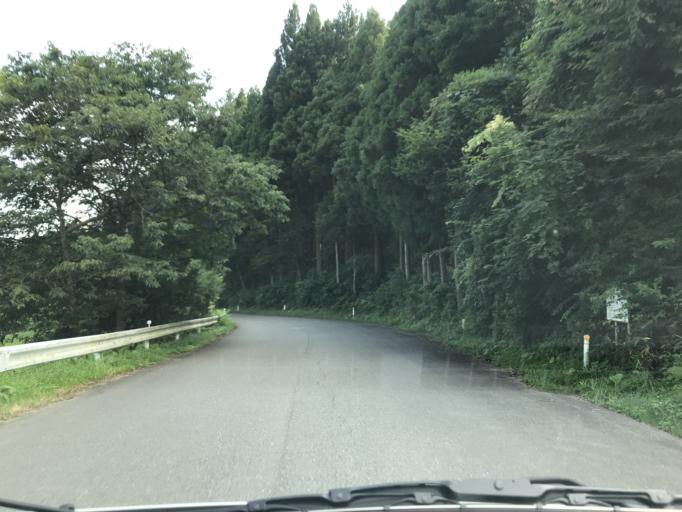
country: JP
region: Iwate
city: Ofunato
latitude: 38.9610
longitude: 141.4715
